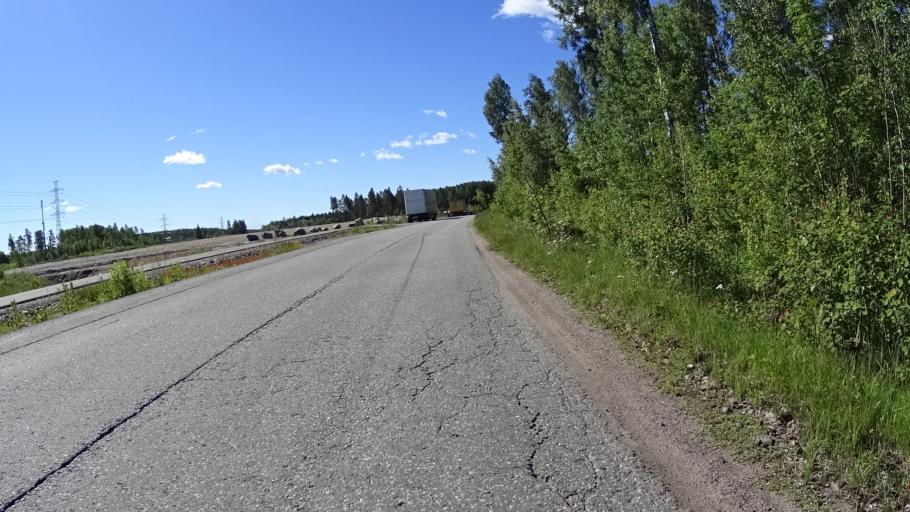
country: FI
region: Uusimaa
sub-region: Helsinki
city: Kilo
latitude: 60.3117
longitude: 24.8384
